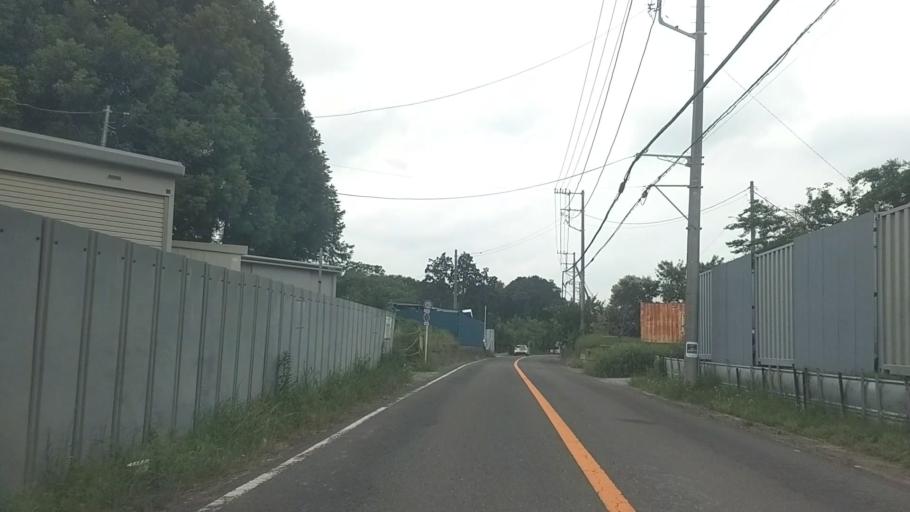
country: JP
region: Kanagawa
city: Fujisawa
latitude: 35.3552
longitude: 139.4351
